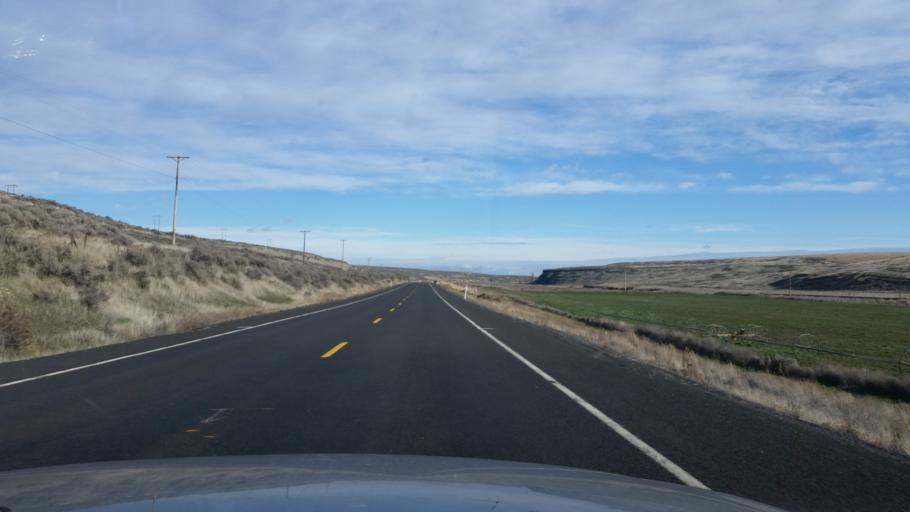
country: US
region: Washington
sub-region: Adams County
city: Ritzville
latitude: 47.3530
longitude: -118.5346
